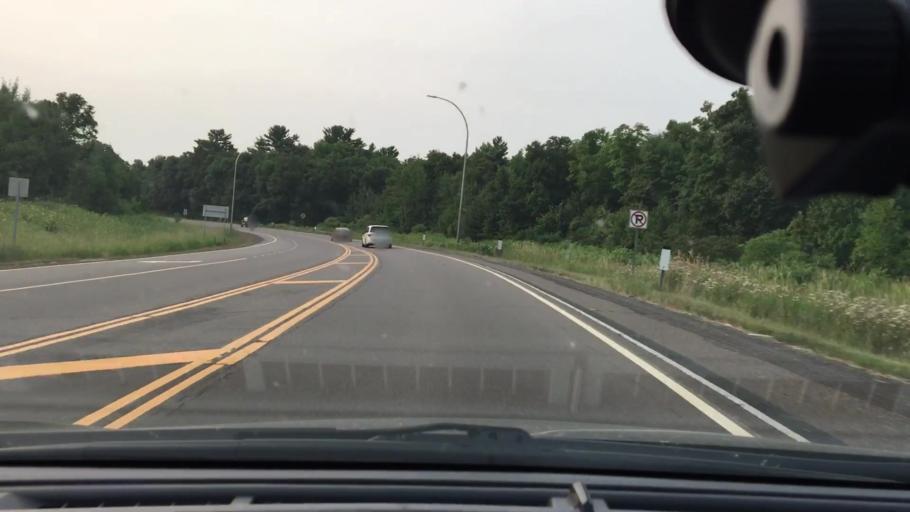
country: US
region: Minnesota
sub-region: Mille Lacs County
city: Vineland
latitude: 46.1103
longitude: -93.6455
